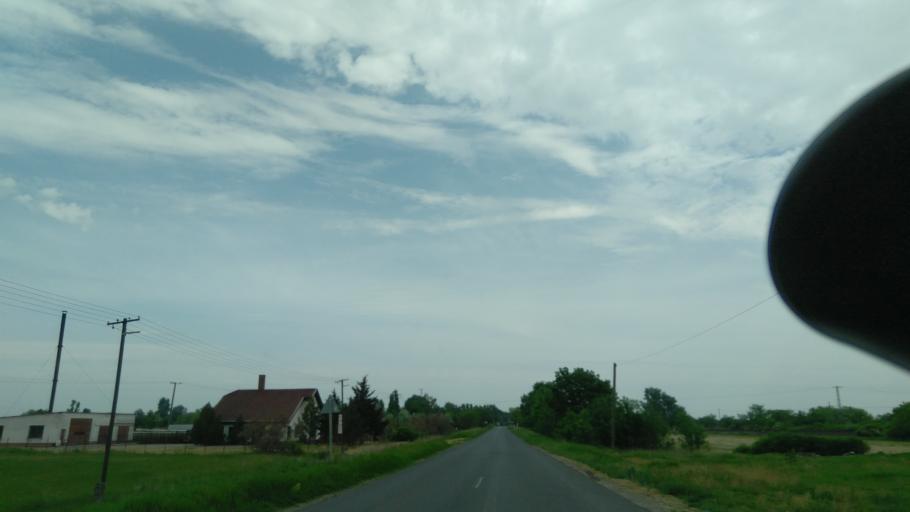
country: HU
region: Bekes
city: Fuzesgyarmat
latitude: 47.0873
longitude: 21.2003
